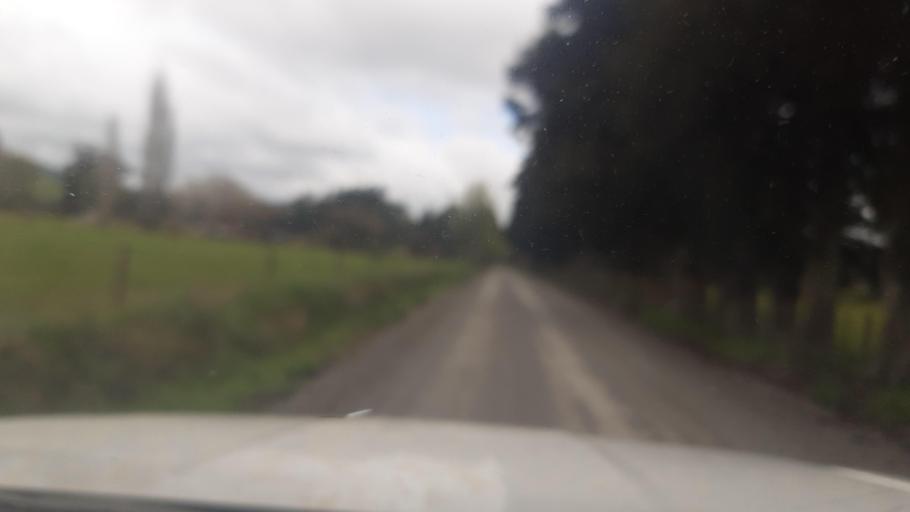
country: NZ
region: Northland
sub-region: Far North District
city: Taipa
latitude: -35.0791
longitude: 173.5136
